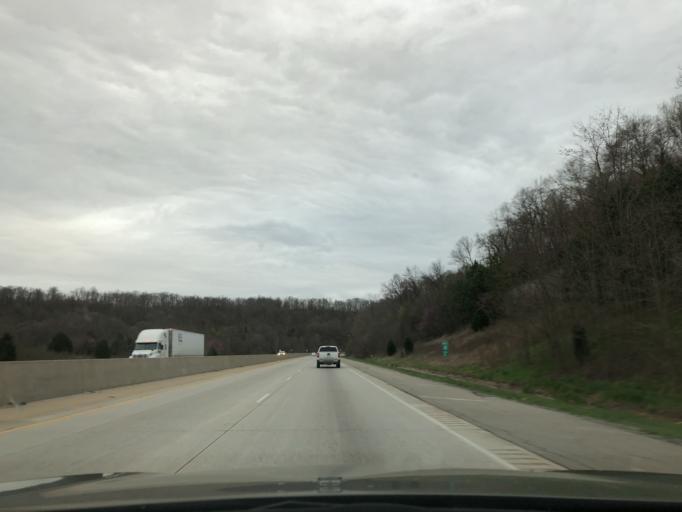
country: US
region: Arkansas
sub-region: Washington County
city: West Fork
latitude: 35.7765
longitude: -94.1864
